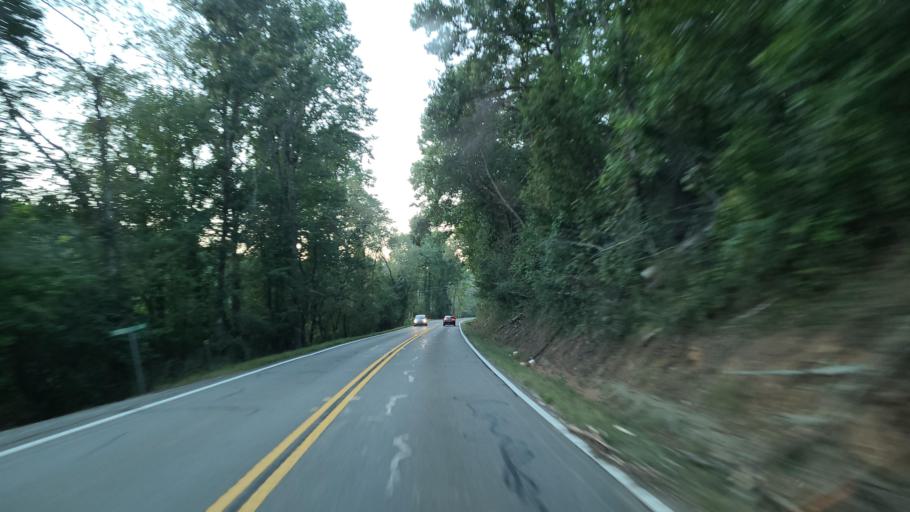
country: US
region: Georgia
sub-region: Gilmer County
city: Ellijay
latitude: 34.7092
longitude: -84.4964
